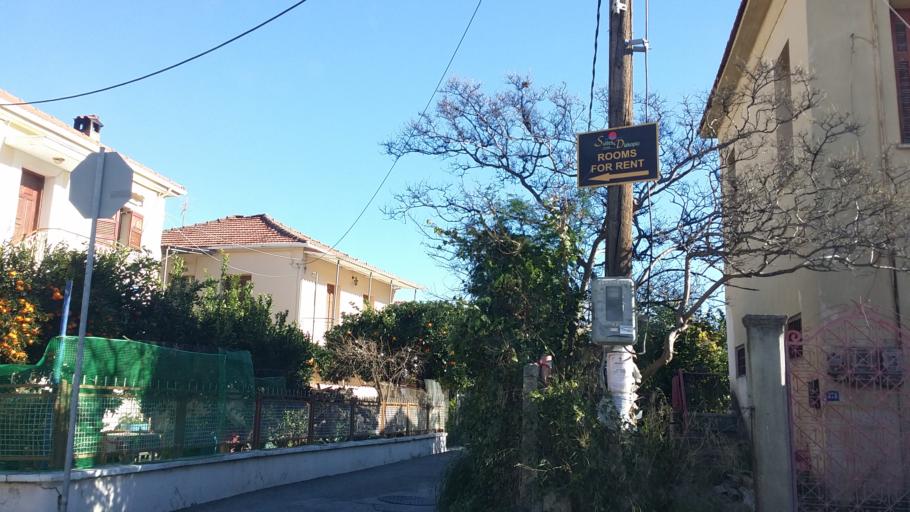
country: GR
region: West Greece
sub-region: Nomos Achaias
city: Temeni
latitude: 38.1928
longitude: 22.1984
